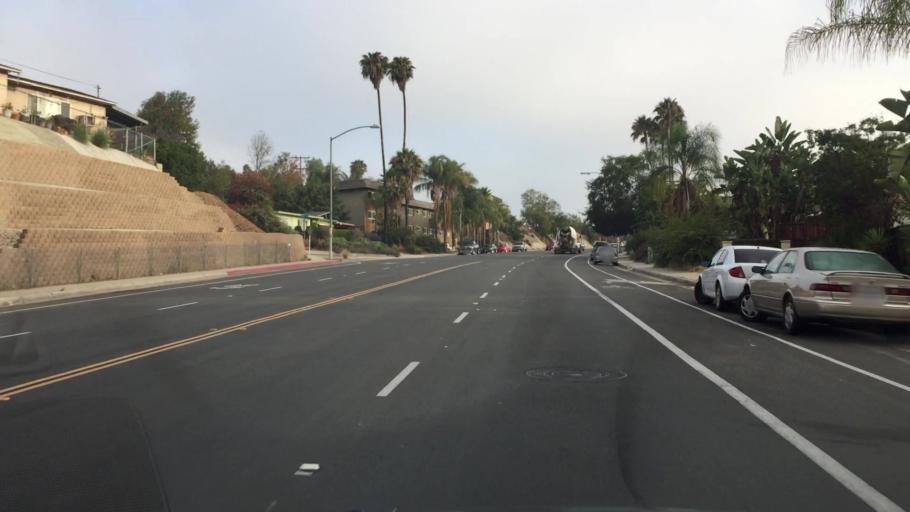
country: US
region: California
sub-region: San Diego County
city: Lemon Grove
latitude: 32.7552
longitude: -117.0656
